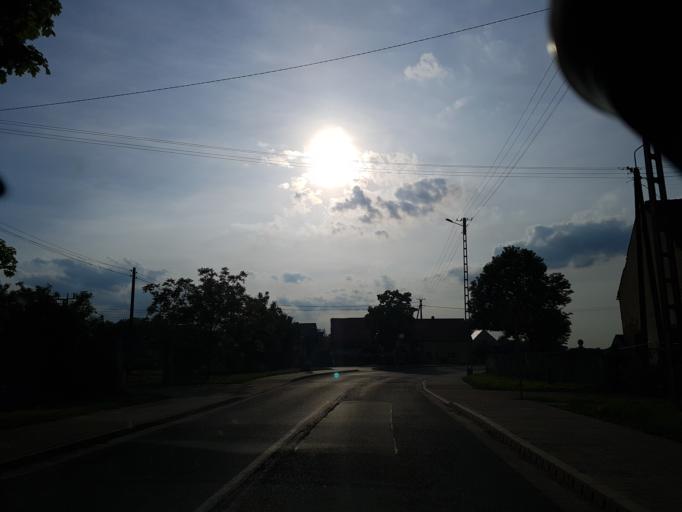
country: PL
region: Lower Silesian Voivodeship
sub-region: Powiat wroclawski
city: Kobierzyce
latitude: 50.9328
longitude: 16.9399
